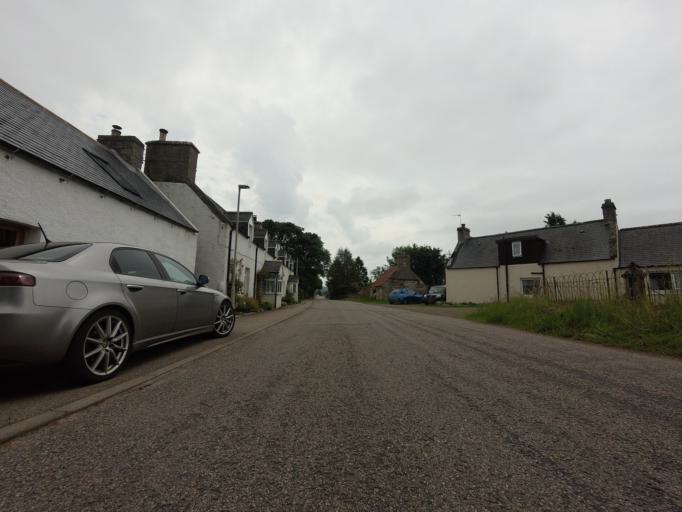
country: GB
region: Scotland
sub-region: Highland
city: Alness
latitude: 57.8858
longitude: -4.3751
